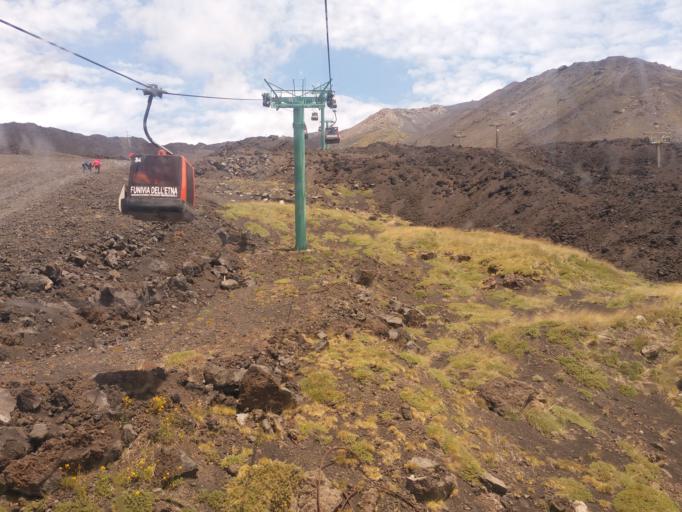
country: IT
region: Sicily
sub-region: Catania
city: Ragalna
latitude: 37.7042
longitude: 14.9992
